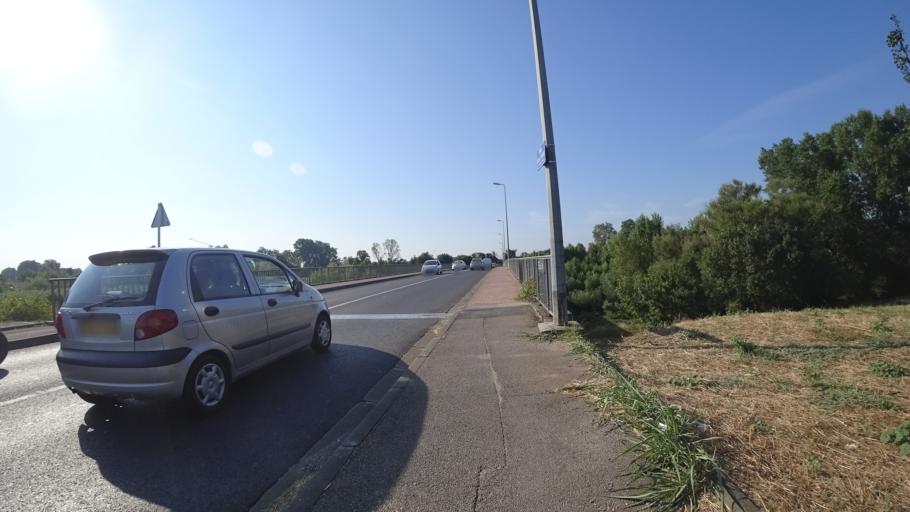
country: FR
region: Languedoc-Roussillon
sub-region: Departement des Pyrenees-Orientales
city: Perpignan
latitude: 42.7091
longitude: 2.9083
